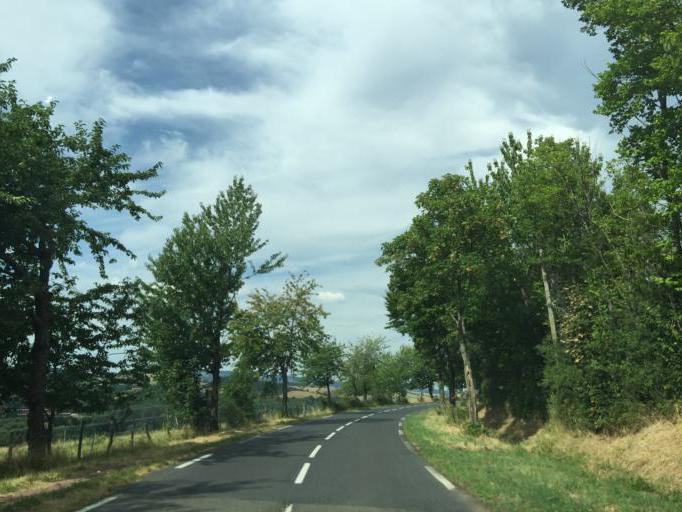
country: FR
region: Rhone-Alpes
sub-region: Departement de la Loire
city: Saint-Jean-Bonnefonds
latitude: 45.4477
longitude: 4.4579
